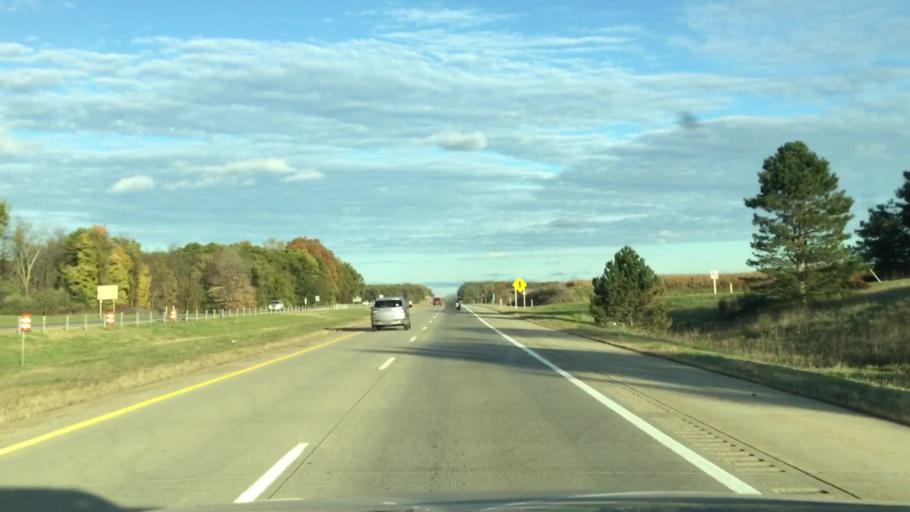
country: US
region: Michigan
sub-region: Calhoun County
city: Marshall
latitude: 42.2830
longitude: -84.8621
